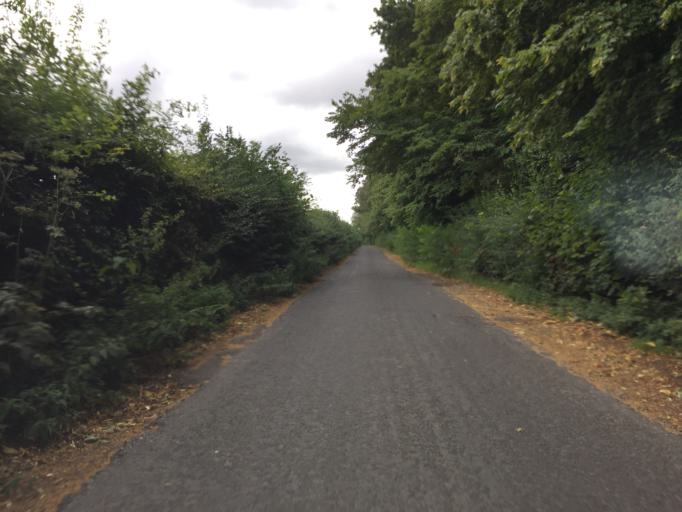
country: GB
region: England
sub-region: Kent
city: Maidstone
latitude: 51.2397
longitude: 0.5342
